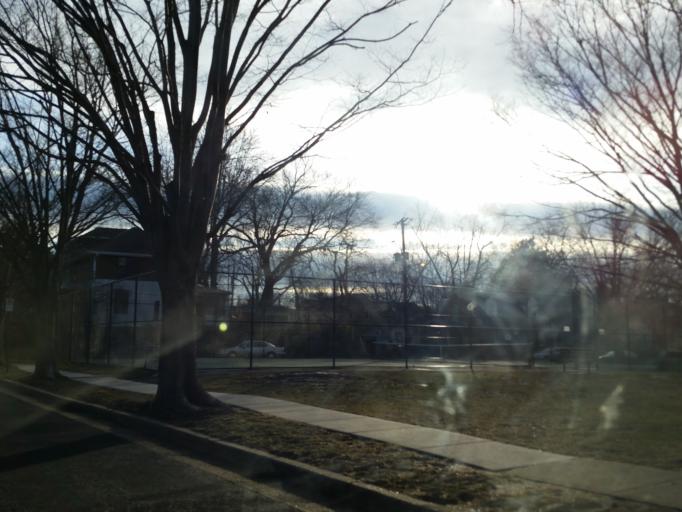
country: US
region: Virginia
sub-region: City of Alexandria
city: Alexandria
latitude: 38.8129
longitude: -77.0616
